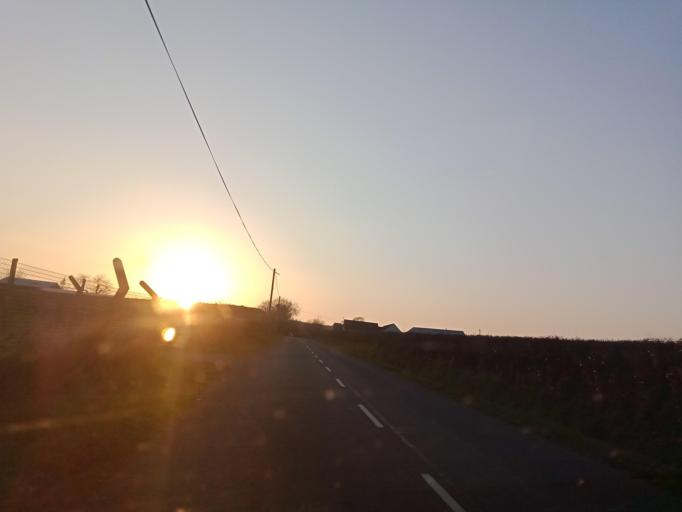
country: IE
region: Leinster
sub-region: Kilkenny
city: Castlecomer
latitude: 52.8393
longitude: -7.2478
